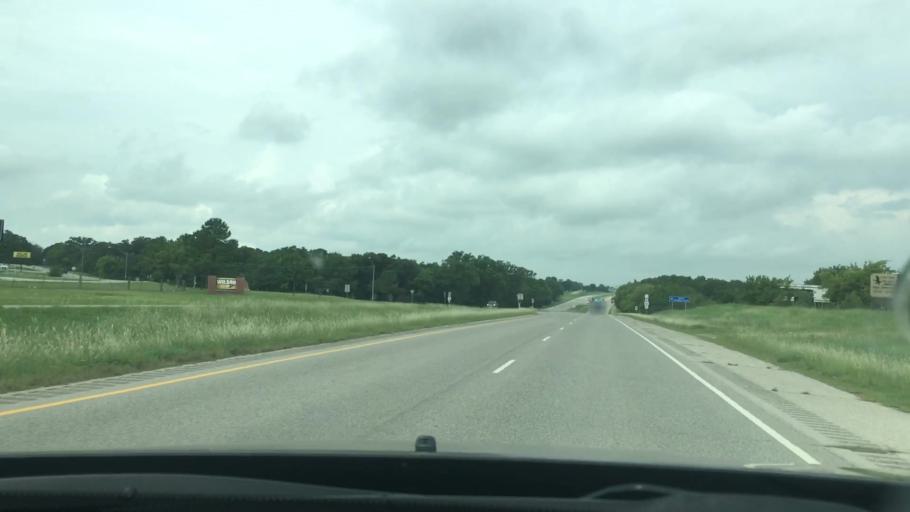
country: US
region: Oklahoma
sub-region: Carter County
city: Wilson
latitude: 34.1730
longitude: -97.4154
